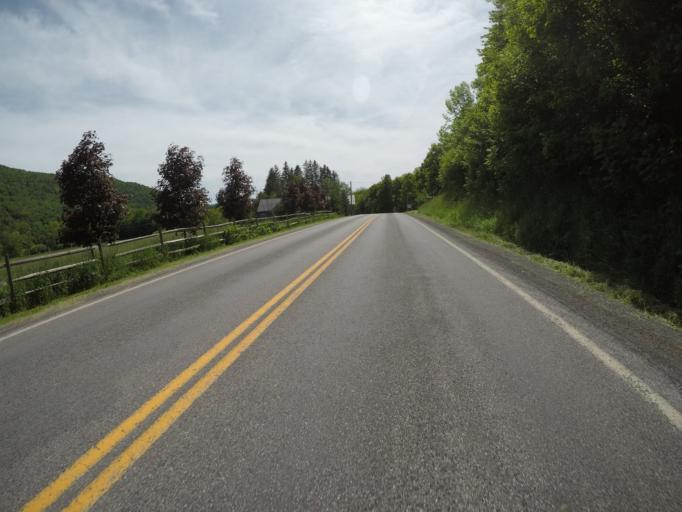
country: US
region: New York
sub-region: Delaware County
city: Delhi
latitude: 42.1240
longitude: -74.8159
